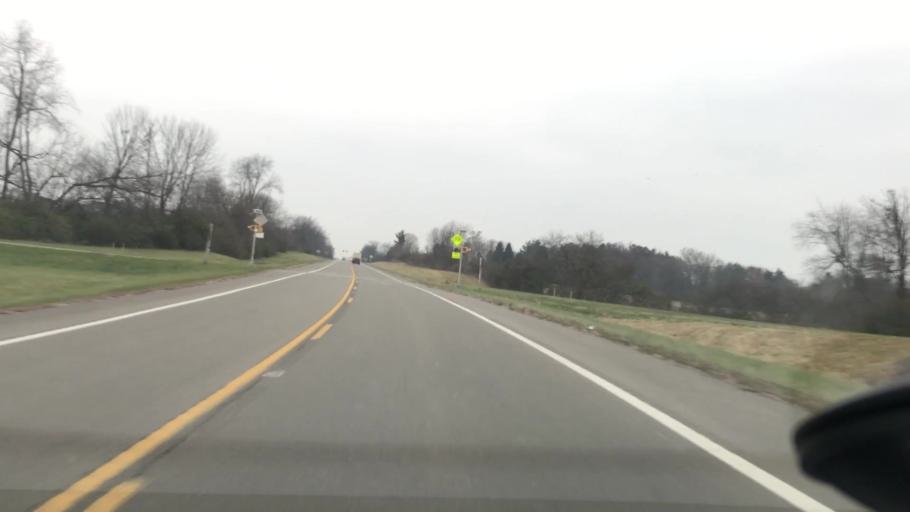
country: US
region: Ohio
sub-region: Clark County
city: Springfield
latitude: 39.8754
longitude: -83.8451
